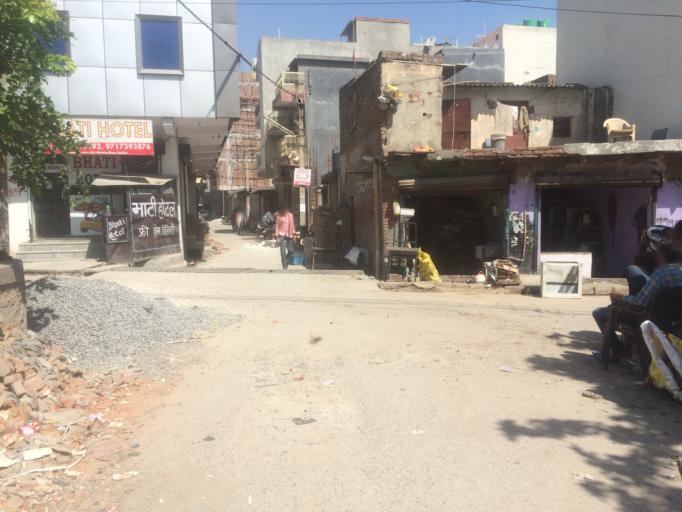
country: IN
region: Uttar Pradesh
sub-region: Gautam Buddha Nagar
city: Noida
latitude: 28.5786
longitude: 77.3608
